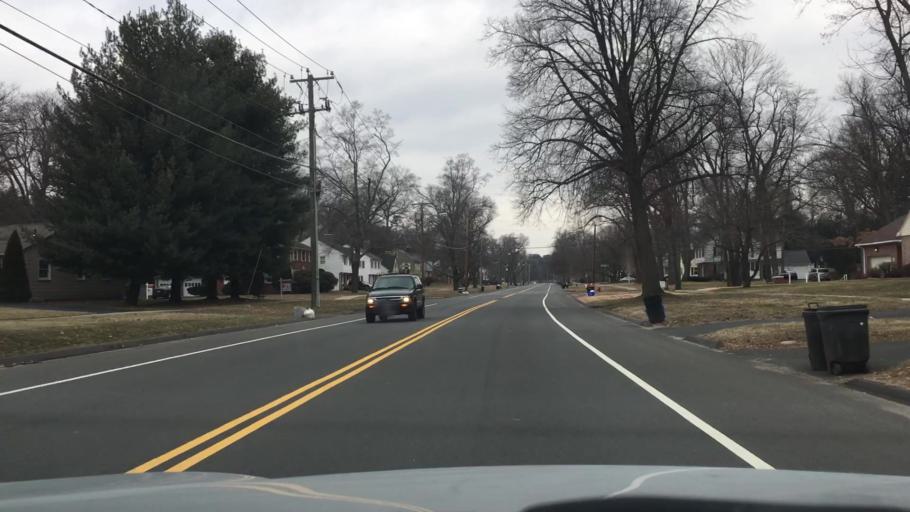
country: US
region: Massachusetts
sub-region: Hampden County
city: Longmeadow
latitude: 42.0508
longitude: -72.5732
